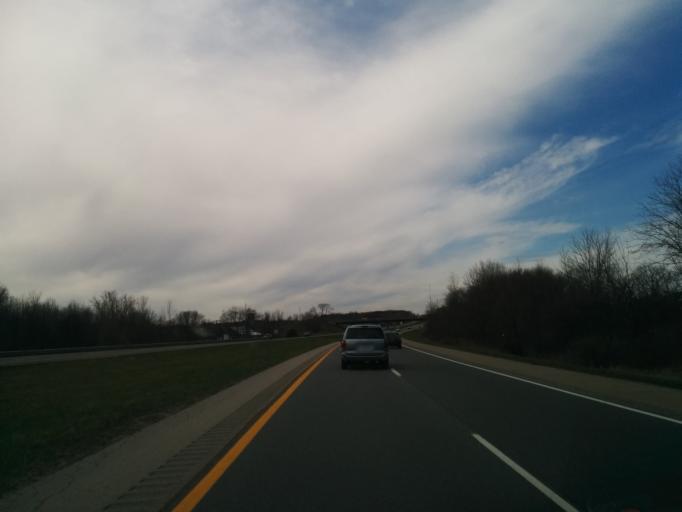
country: US
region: Michigan
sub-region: Ottawa County
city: Zeeland
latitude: 42.7984
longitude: -85.9950
